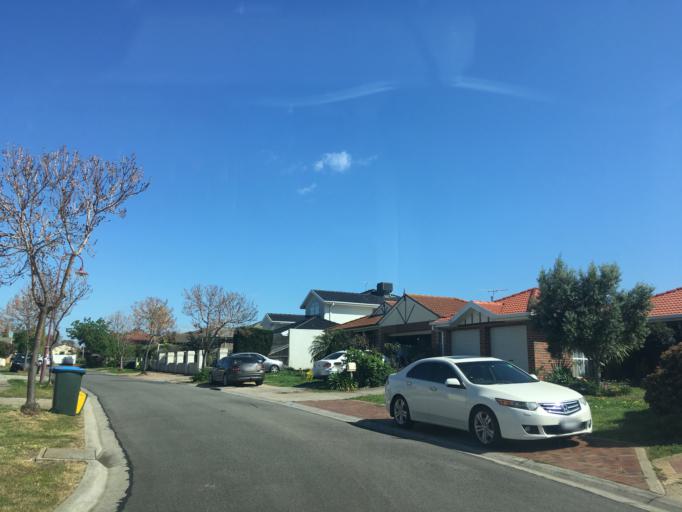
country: AU
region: Victoria
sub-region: Wyndham
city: Hoppers Crossing
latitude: -37.8763
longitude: 144.7040
